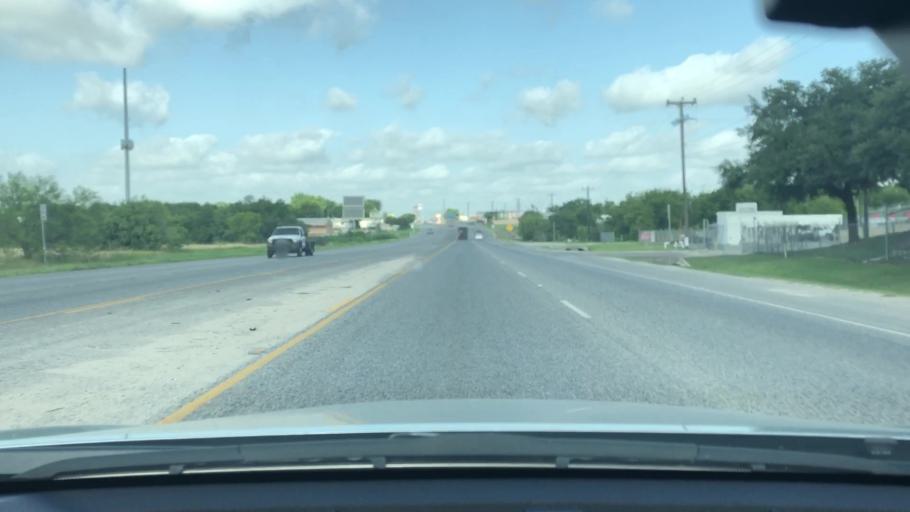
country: US
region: Texas
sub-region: Bexar County
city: Kirby
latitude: 29.4752
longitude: -98.3758
